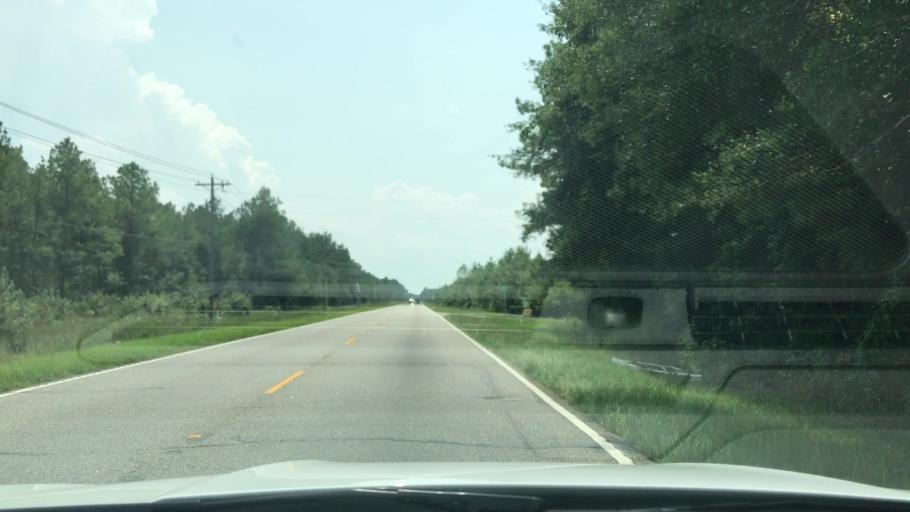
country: US
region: South Carolina
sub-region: Georgetown County
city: Georgetown
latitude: 33.5204
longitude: -79.2461
